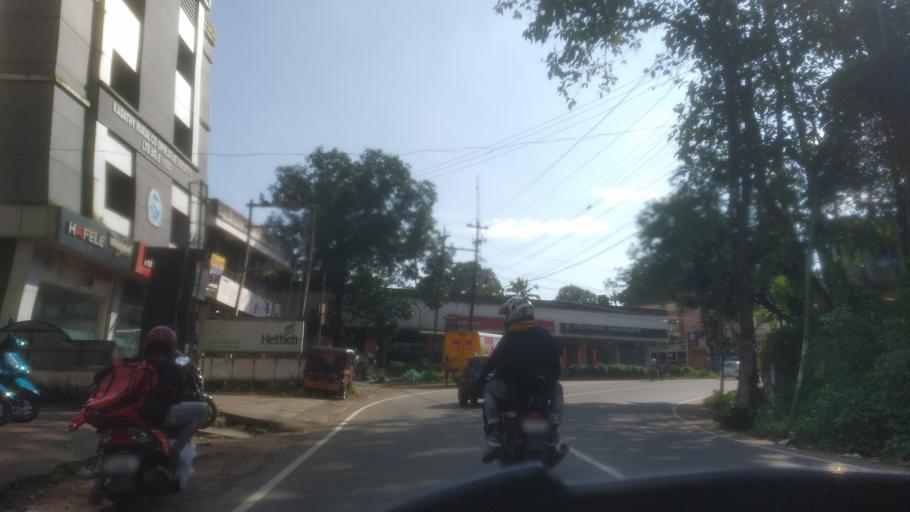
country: IN
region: Kerala
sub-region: Ernakulam
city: Muvattupula
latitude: 9.9889
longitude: 76.5704
